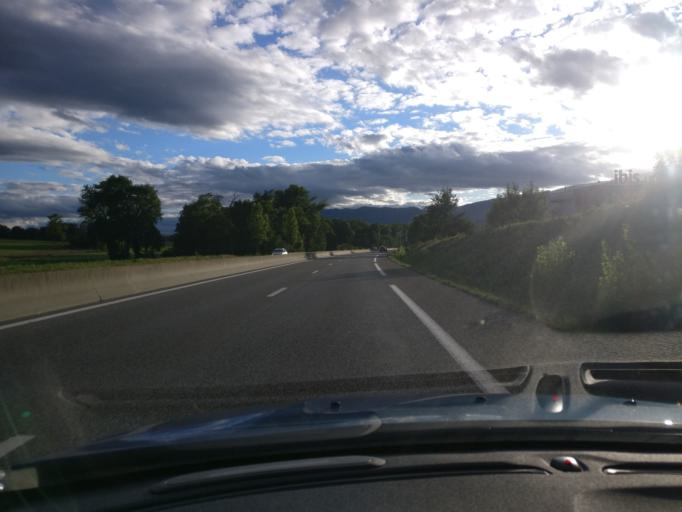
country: FR
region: Rhone-Alpes
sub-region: Departement de l'Ain
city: Saint-Genis-Pouilly
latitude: 46.2353
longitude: 6.0279
